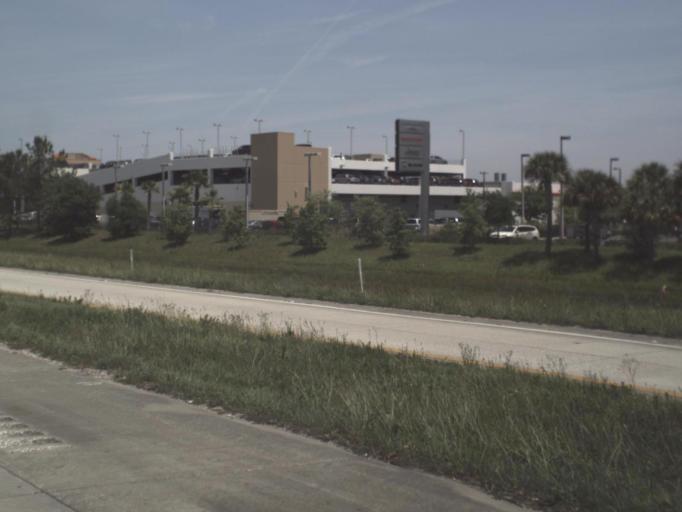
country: US
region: Florida
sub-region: Saint Johns County
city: Ponte Vedra Beach
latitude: 30.2202
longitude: -81.5138
